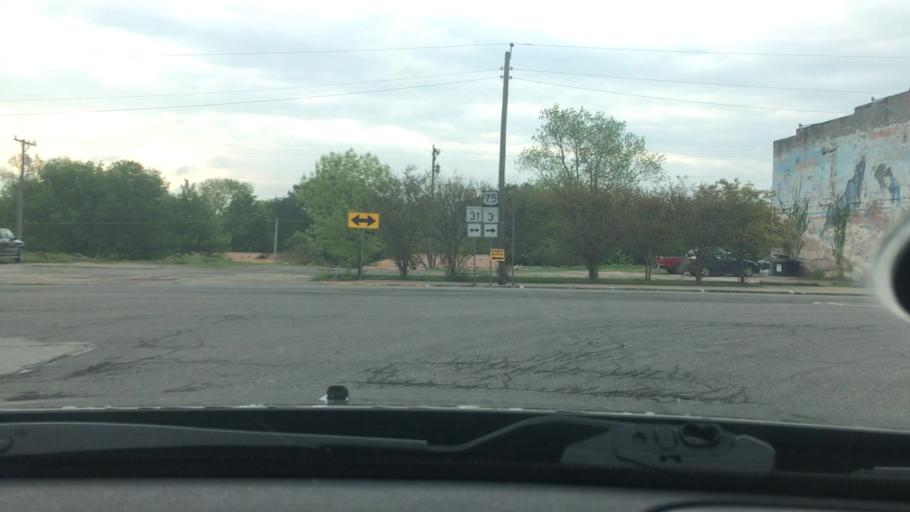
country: US
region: Oklahoma
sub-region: Coal County
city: Coalgate
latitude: 34.5405
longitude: -96.2182
